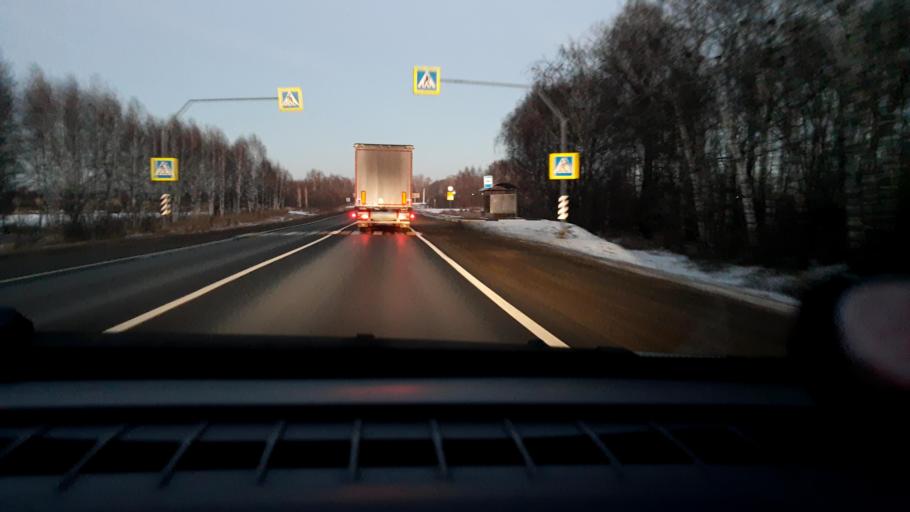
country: RU
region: Nizjnij Novgorod
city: Lyskovo
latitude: 56.0068
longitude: 44.8974
